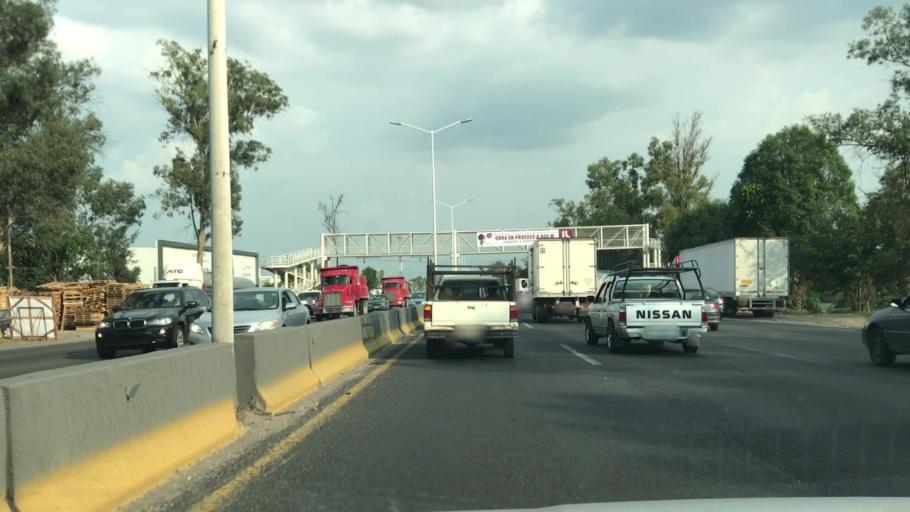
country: MX
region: Jalisco
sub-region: Tlajomulco de Zuniga
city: La Tijera
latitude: 20.6217
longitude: -103.4308
